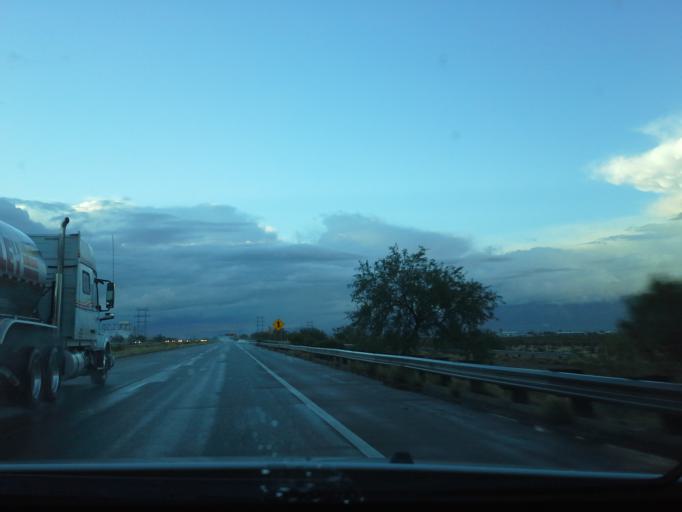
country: US
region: Arizona
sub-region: Pima County
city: Tucson
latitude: 32.1364
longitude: -110.8885
